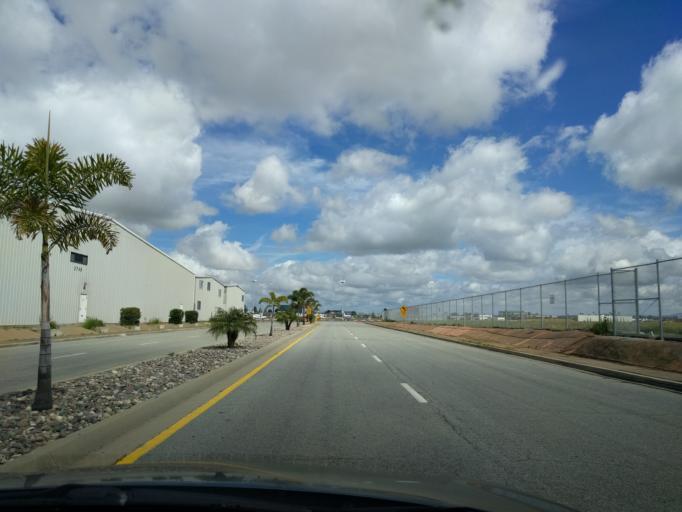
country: US
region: California
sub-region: San Diego County
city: San Diego
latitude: 32.8113
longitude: -117.1401
